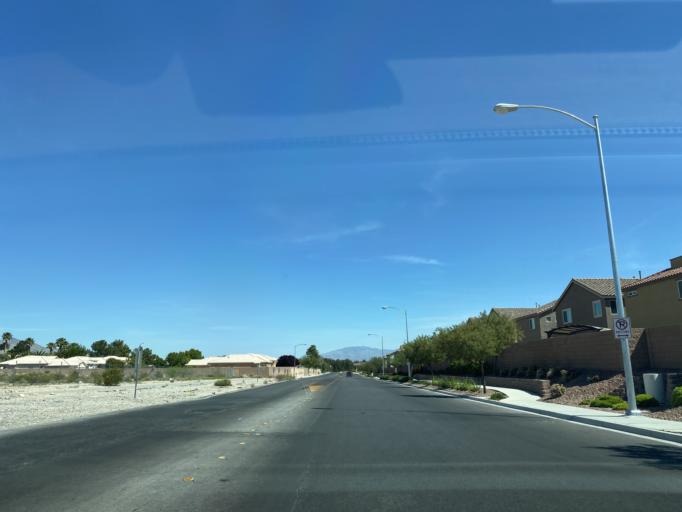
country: US
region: Nevada
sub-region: Clark County
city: Spring Valley
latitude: 36.0873
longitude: -115.2610
